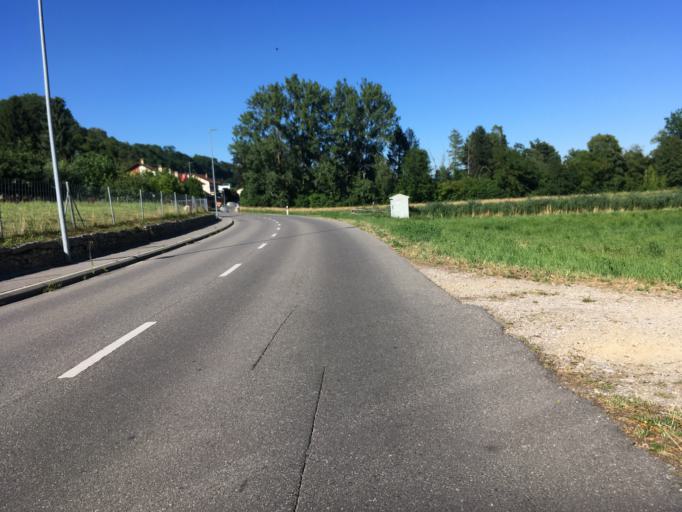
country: CH
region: Vaud
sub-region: Broye-Vully District
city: Avenches
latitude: 46.9284
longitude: 7.0416
